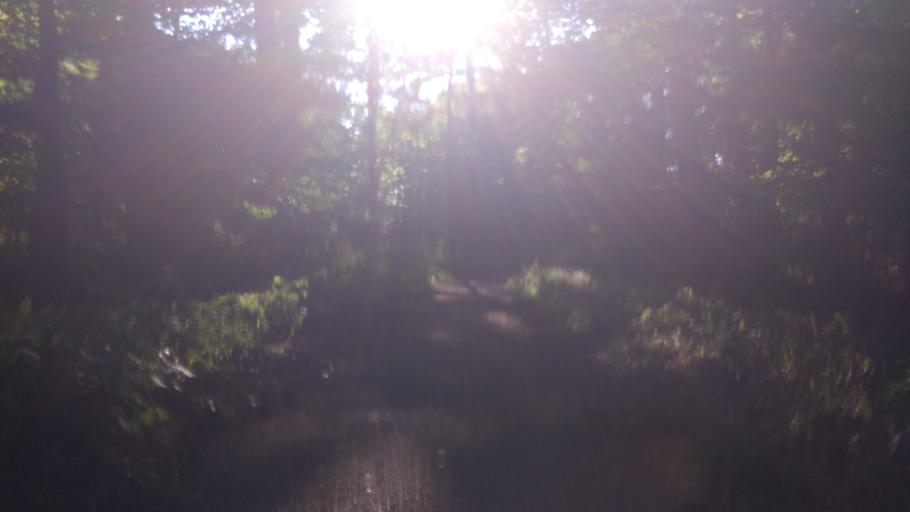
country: FR
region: Alsace
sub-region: Departement du Bas-Rhin
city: Bischwiller
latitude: 48.7603
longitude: 7.8421
